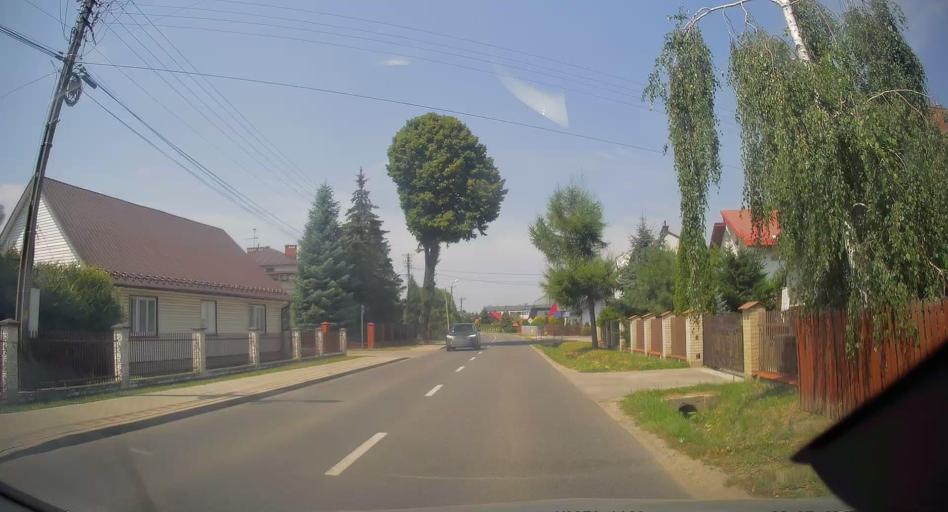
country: PL
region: Subcarpathian Voivodeship
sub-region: Powiat debicki
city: Debica
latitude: 50.0441
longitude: 21.4309
